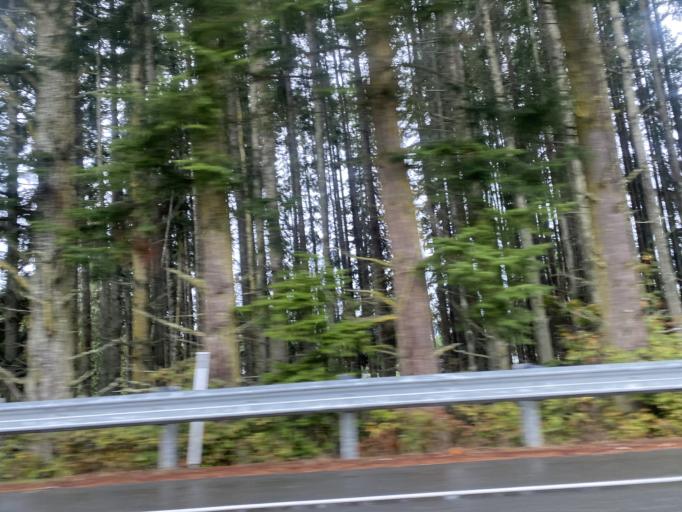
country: US
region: Washington
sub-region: Island County
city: Langley
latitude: 48.0485
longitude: -122.4421
